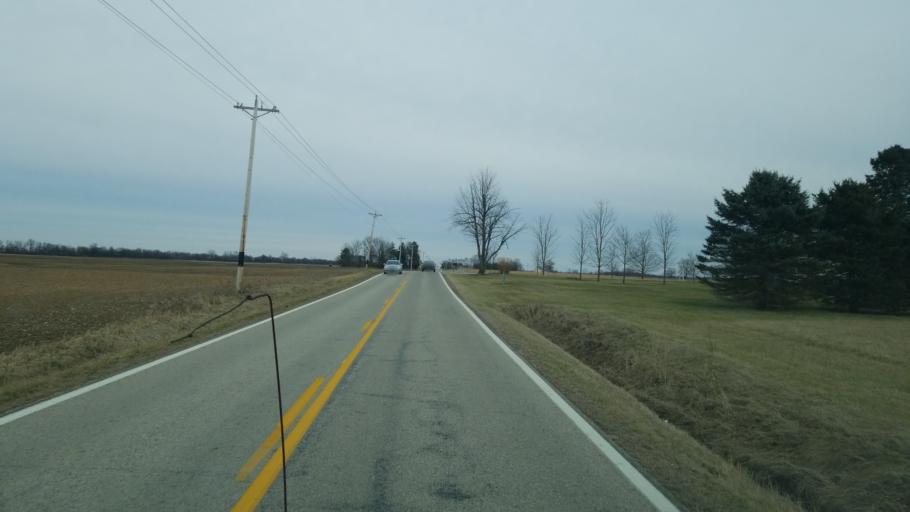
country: US
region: Ohio
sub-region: Pickaway County
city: Williamsport
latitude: 39.5692
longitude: -83.0619
